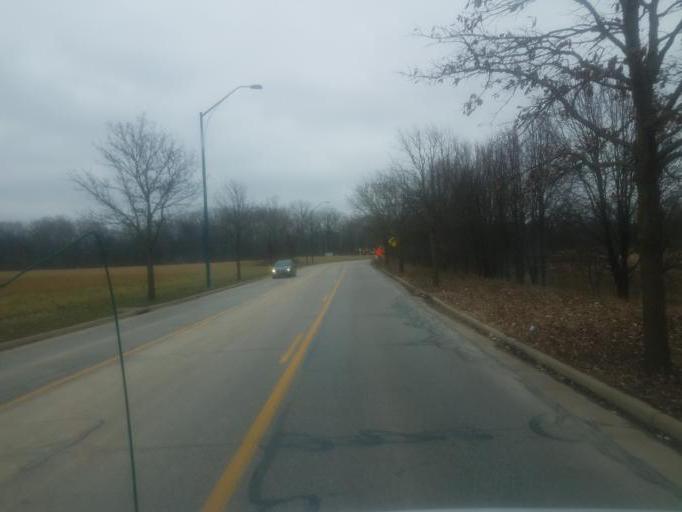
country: US
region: Ohio
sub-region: Franklin County
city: Westerville
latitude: 40.1208
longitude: -82.9429
